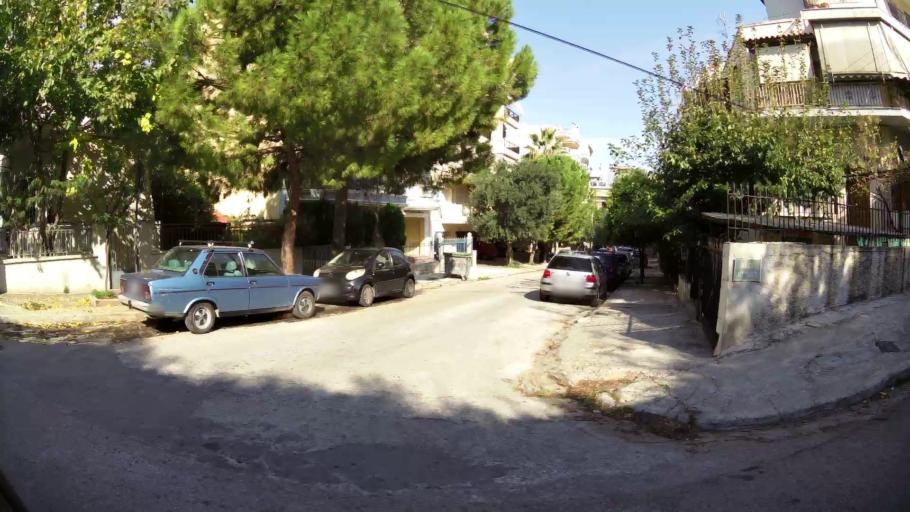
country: GR
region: Attica
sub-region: Nomarchia Athinas
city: Nea Ionia
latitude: 38.0322
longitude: 23.7666
